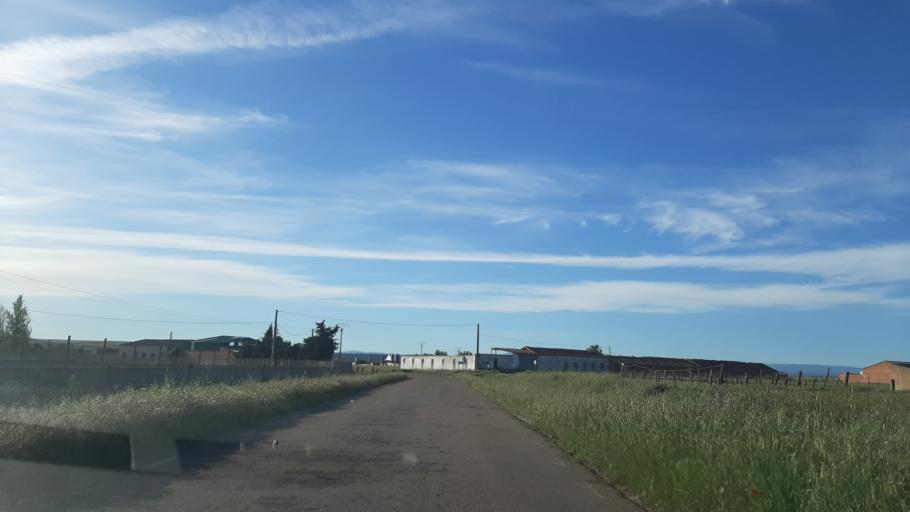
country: ES
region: Castille and Leon
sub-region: Provincia de Salamanca
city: Pedrosillo de Alba
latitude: 40.8212
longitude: -5.3970
